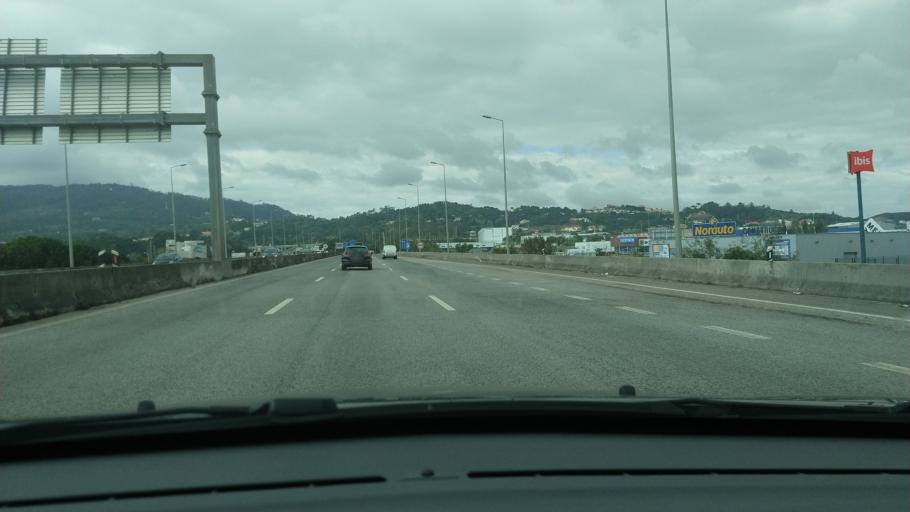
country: PT
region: Lisbon
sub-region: Sintra
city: Rio de Mouro
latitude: 38.7793
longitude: -9.3534
